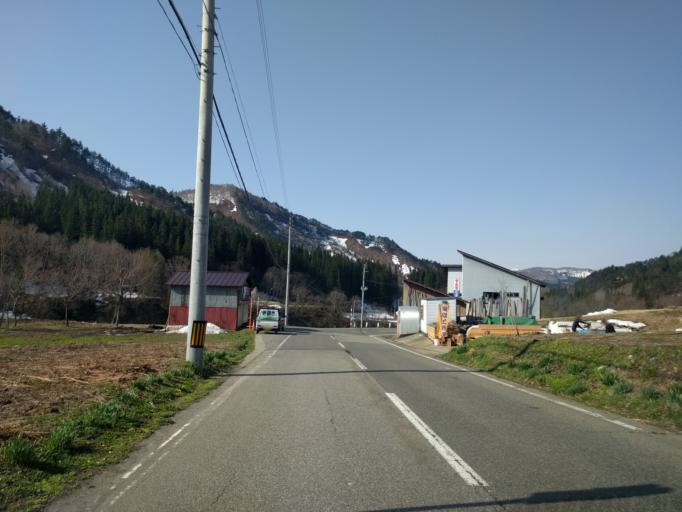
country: JP
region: Niigata
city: Muramatsu
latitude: 37.3232
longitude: 139.4663
